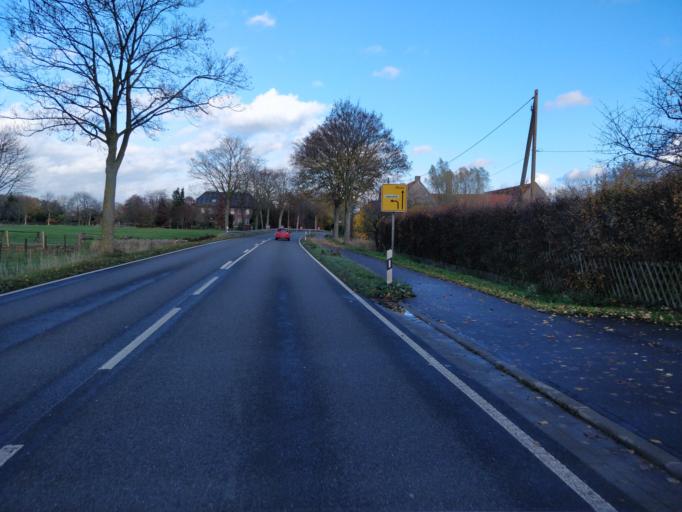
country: DE
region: North Rhine-Westphalia
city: Rees
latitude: 51.7746
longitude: 6.4188
